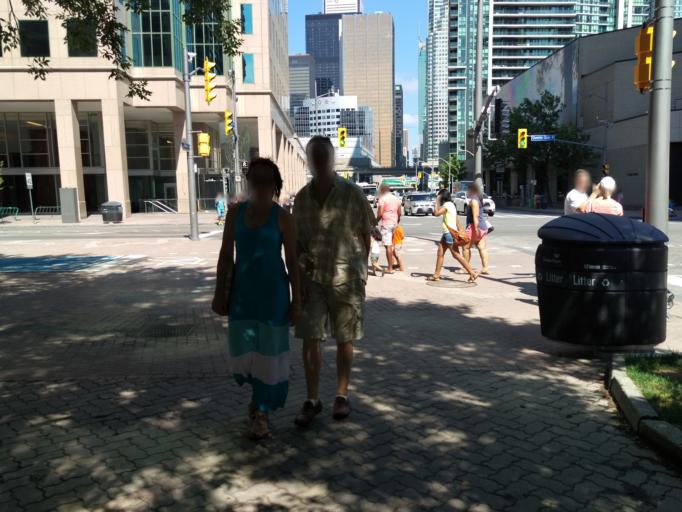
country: CA
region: Ontario
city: Toronto
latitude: 43.6409
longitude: -79.3769
